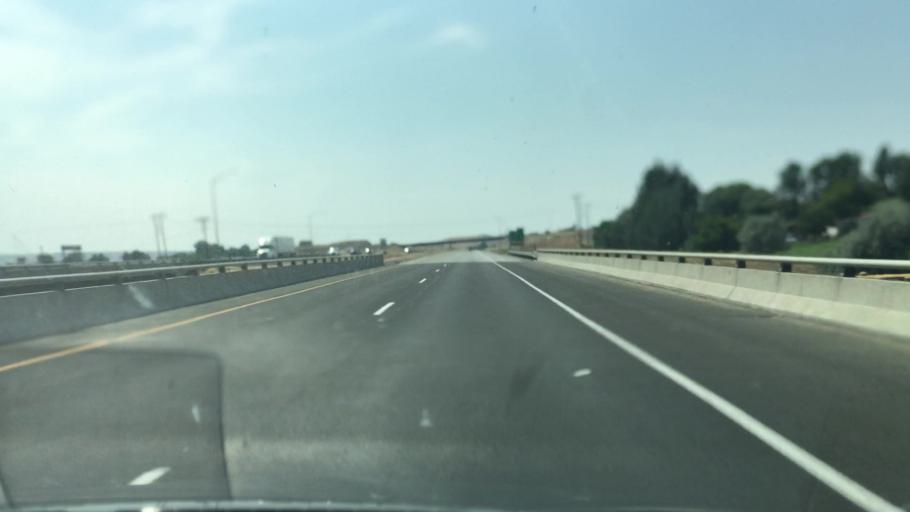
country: US
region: Idaho
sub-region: Elmore County
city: Glenns Ferry
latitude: 42.9607
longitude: -115.2810
